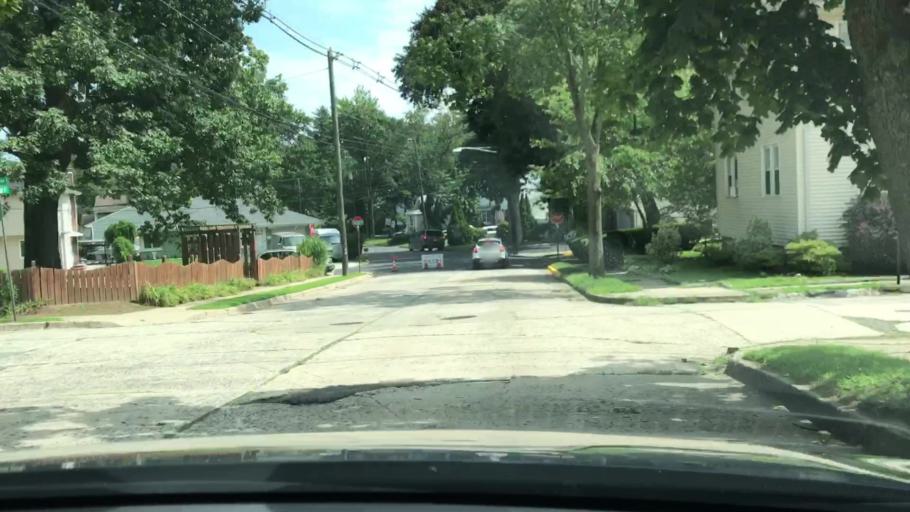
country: US
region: New Jersey
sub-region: Bergen County
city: Bergenfield
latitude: 40.9202
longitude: -74.0055
